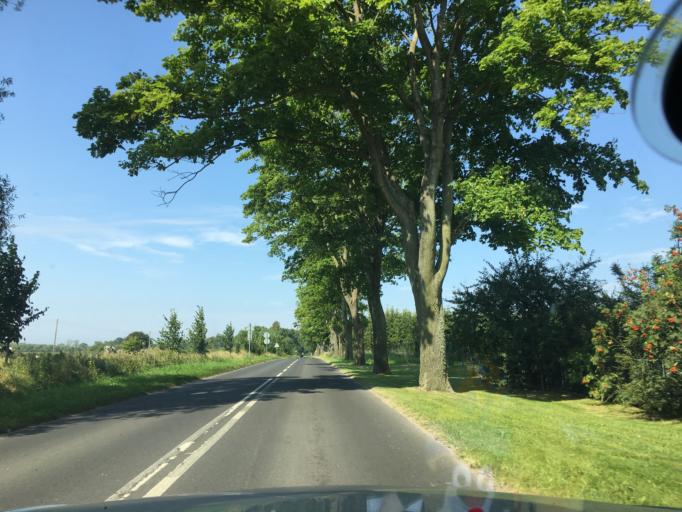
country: PL
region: West Pomeranian Voivodeship
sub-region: Powiat gryficki
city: Pobierowo
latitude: 54.0129
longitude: 14.8631
